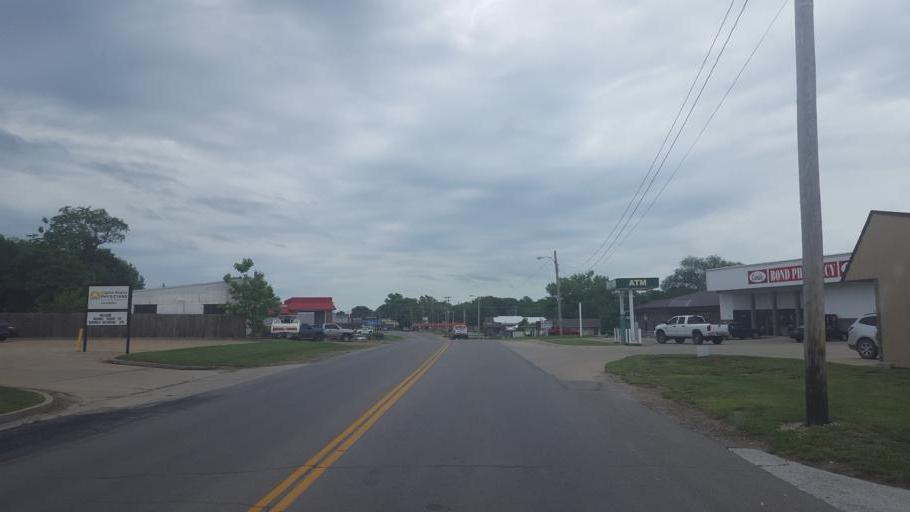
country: US
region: Missouri
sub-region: Moniteau County
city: California
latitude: 38.6284
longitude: -92.5760
